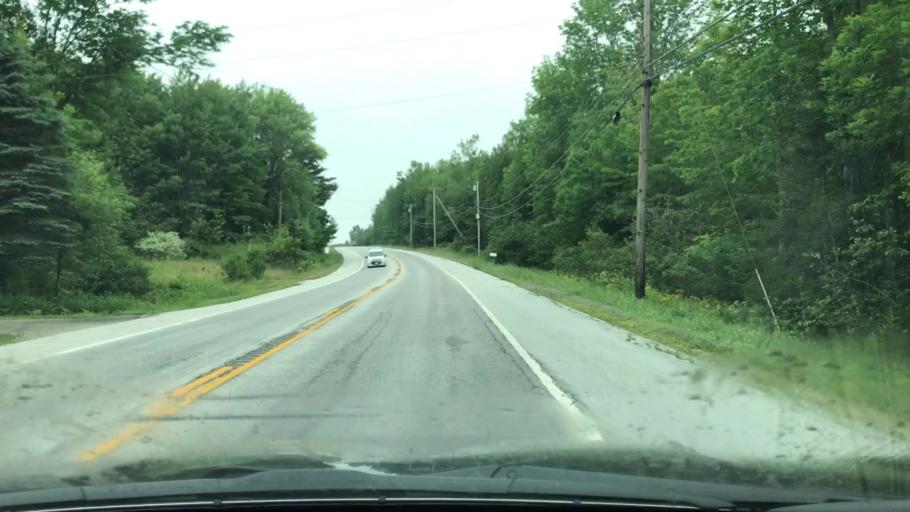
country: US
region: Maine
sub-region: Waldo County
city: Northport
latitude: 44.3239
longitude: -68.9619
